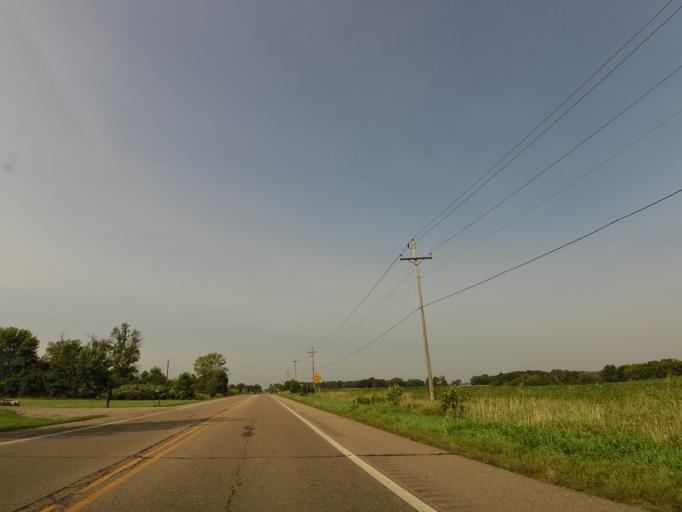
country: US
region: Minnesota
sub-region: Carver County
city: Young America (historical)
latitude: 44.7671
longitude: -93.8668
